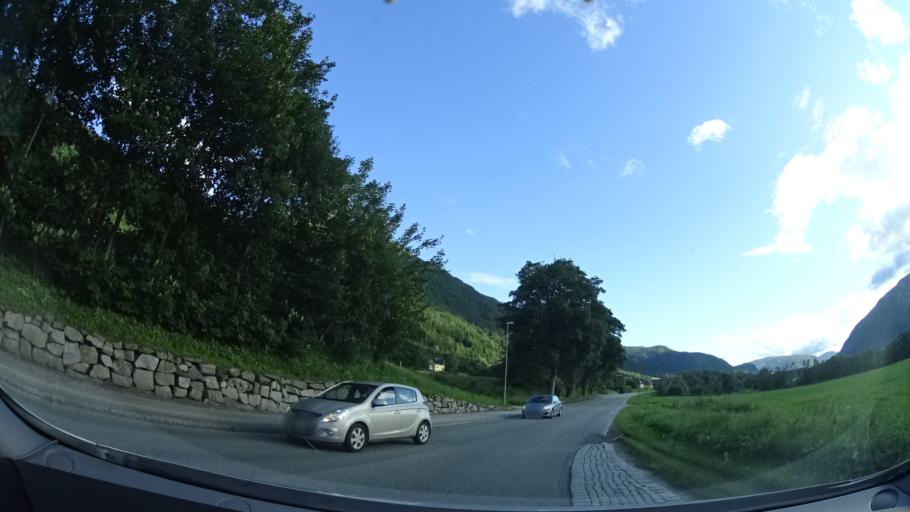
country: NO
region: More og Romsdal
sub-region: Gjemnes
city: Batnfjordsora
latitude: 62.8914
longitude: 7.6793
